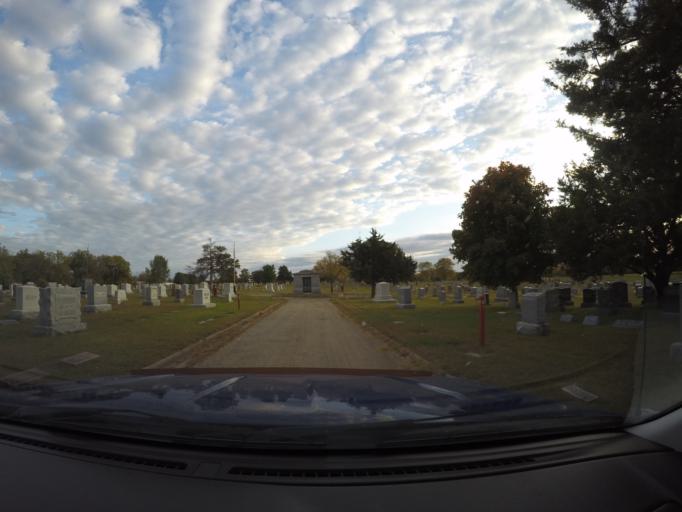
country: US
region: Kansas
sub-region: Shawnee County
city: Topeka
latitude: 39.0390
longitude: -95.6519
